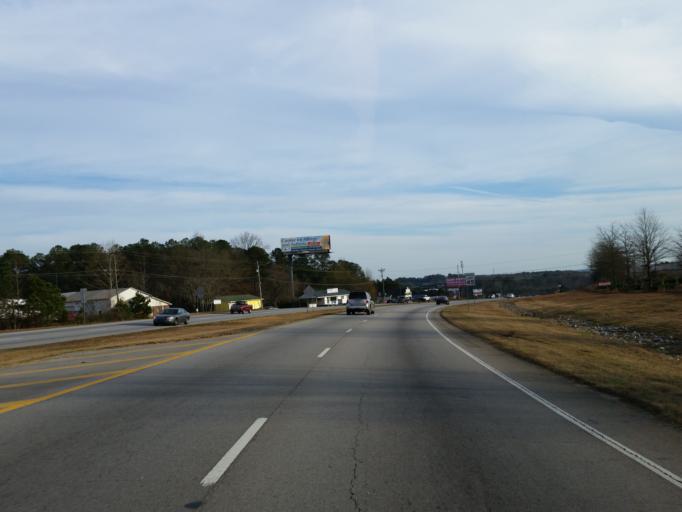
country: US
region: Georgia
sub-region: Paulding County
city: Hiram
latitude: 33.9013
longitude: -84.7707
